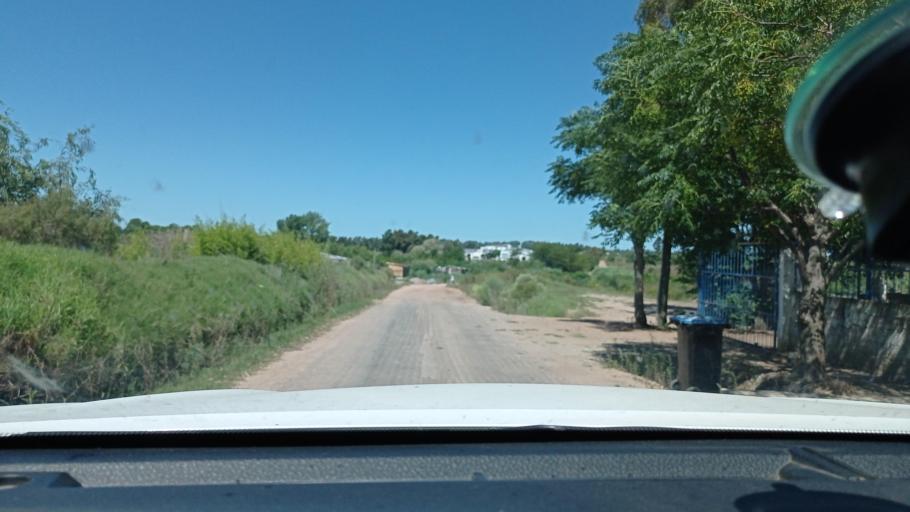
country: UY
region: Canelones
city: Las Piedras
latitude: -34.7416
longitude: -56.2131
